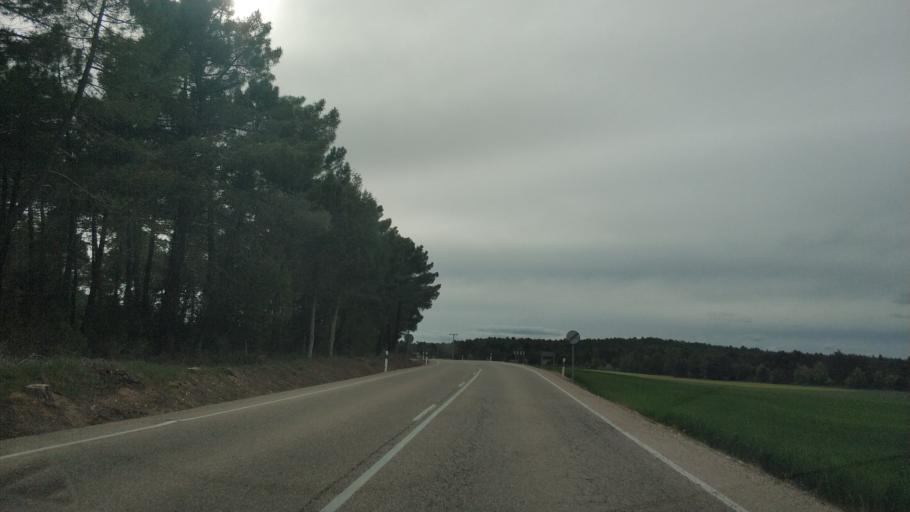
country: ES
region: Castille and Leon
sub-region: Provincia de Soria
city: Bayubas de Abajo
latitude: 41.5075
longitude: -2.9063
